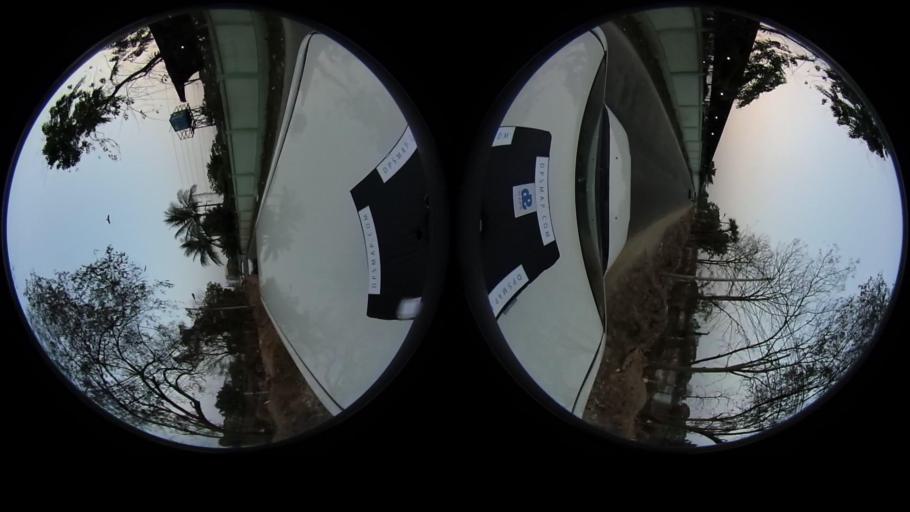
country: MM
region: Yangon
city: Yangon
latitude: 16.7814
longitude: 96.1893
